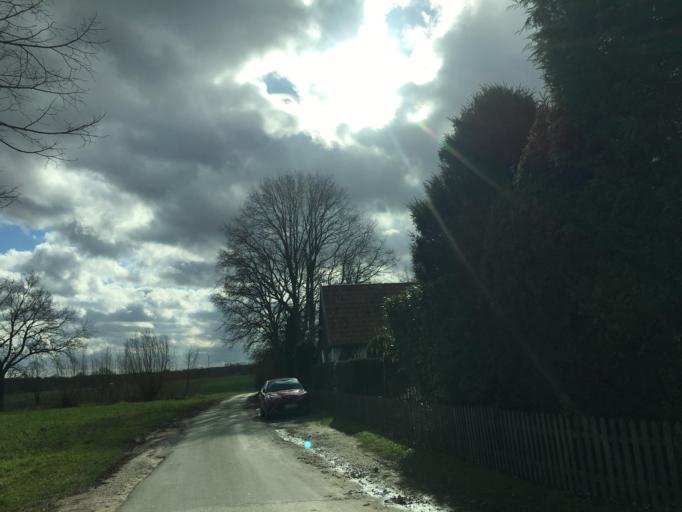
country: DE
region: North Rhine-Westphalia
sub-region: Regierungsbezirk Munster
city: Horstmar
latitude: 52.0865
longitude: 7.3168
